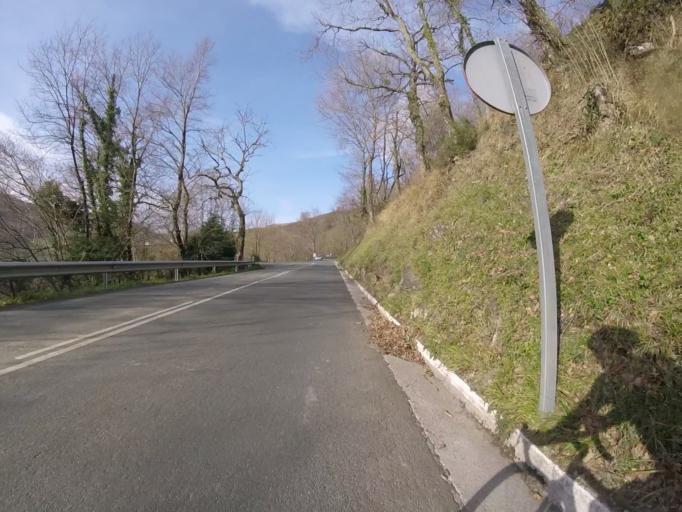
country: ES
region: Basque Country
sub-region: Provincia de Guipuzcoa
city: Larraul
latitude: 43.2038
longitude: -2.1221
